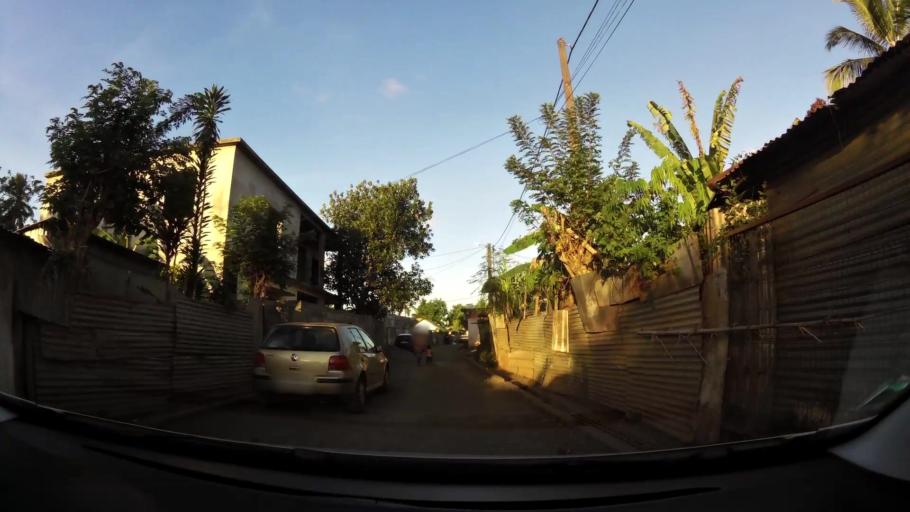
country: YT
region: Dembeni
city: Dembeni
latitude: -12.8434
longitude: 45.1911
